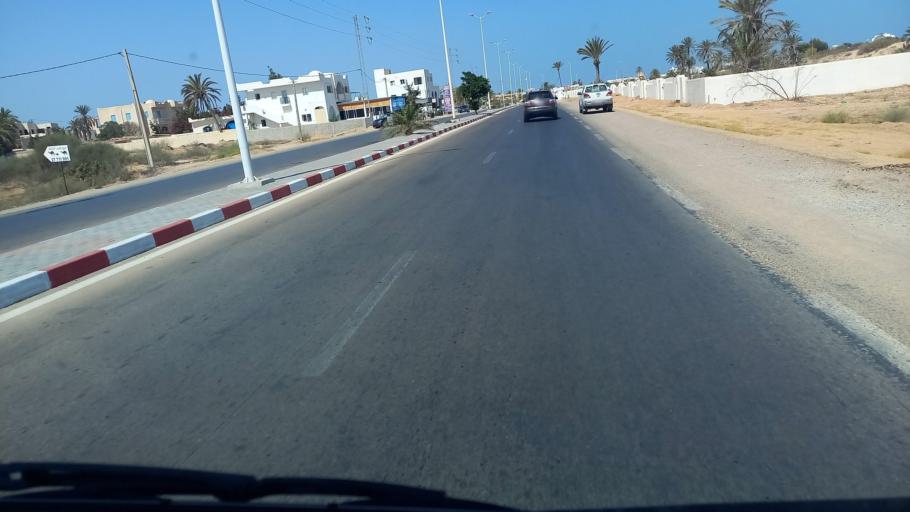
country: TN
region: Madanin
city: Midoun
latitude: 33.8612
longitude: 10.9680
